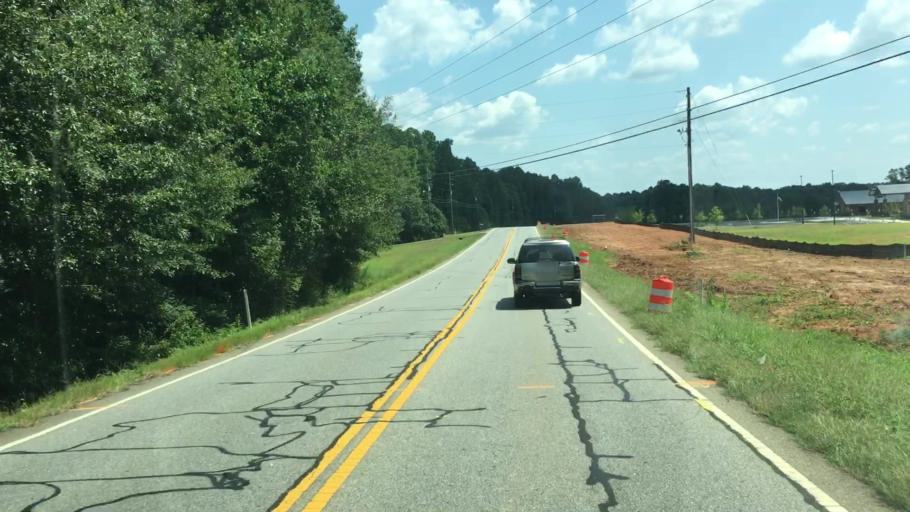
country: US
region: Georgia
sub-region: Barrow County
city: Statham
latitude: 33.9209
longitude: -83.6084
